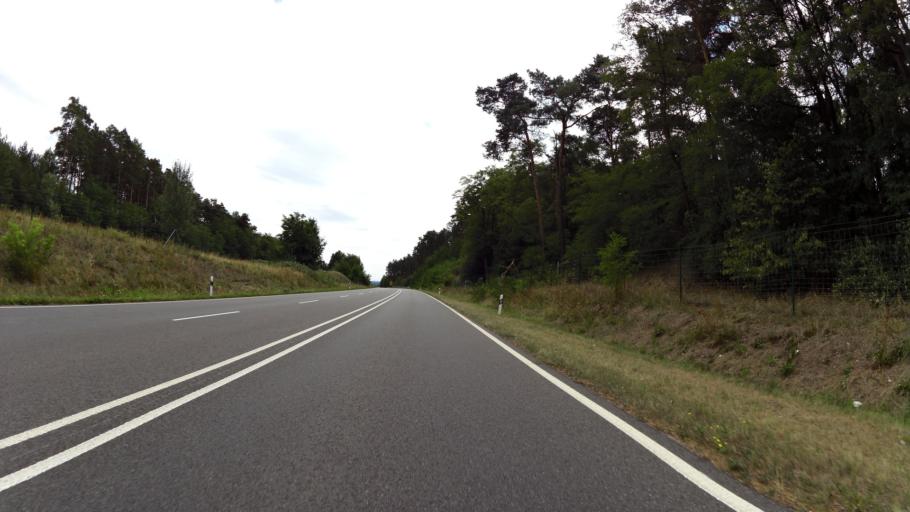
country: DE
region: Brandenburg
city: Neuzelle
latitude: 52.0216
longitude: 14.6778
